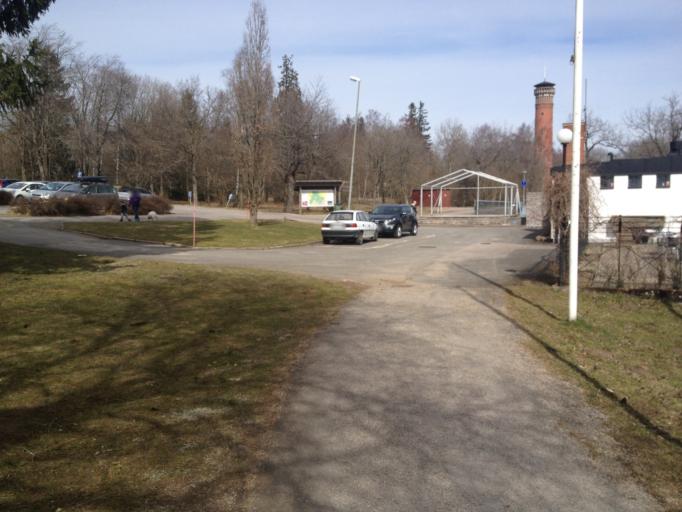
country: SE
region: Vaestra Goetaland
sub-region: Falkopings Kommun
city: Falkoeping
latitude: 58.1828
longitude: 13.5399
